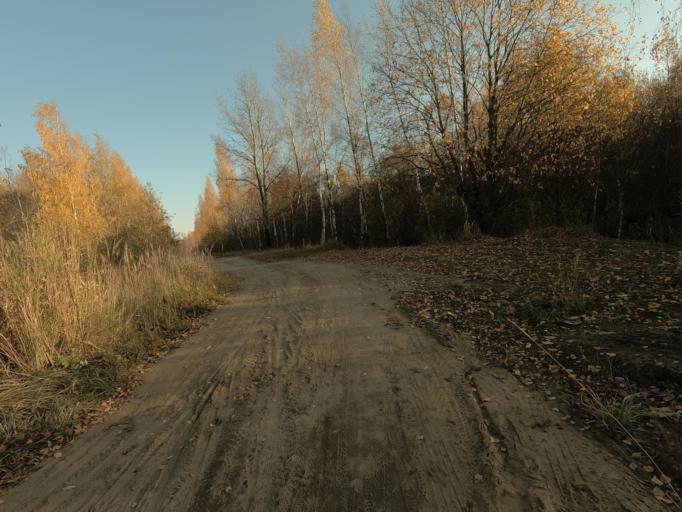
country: RU
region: Leningrad
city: Kirovsk
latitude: 59.8644
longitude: 31.0130
